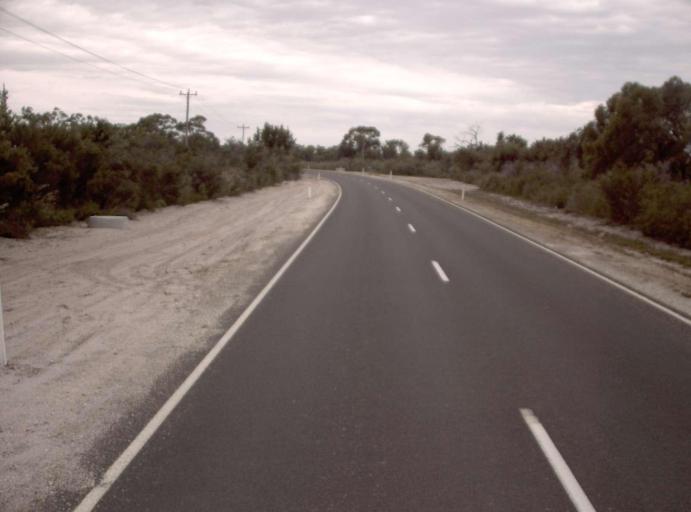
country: AU
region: Victoria
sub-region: Wellington
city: Sale
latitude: -38.1824
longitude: 147.3752
